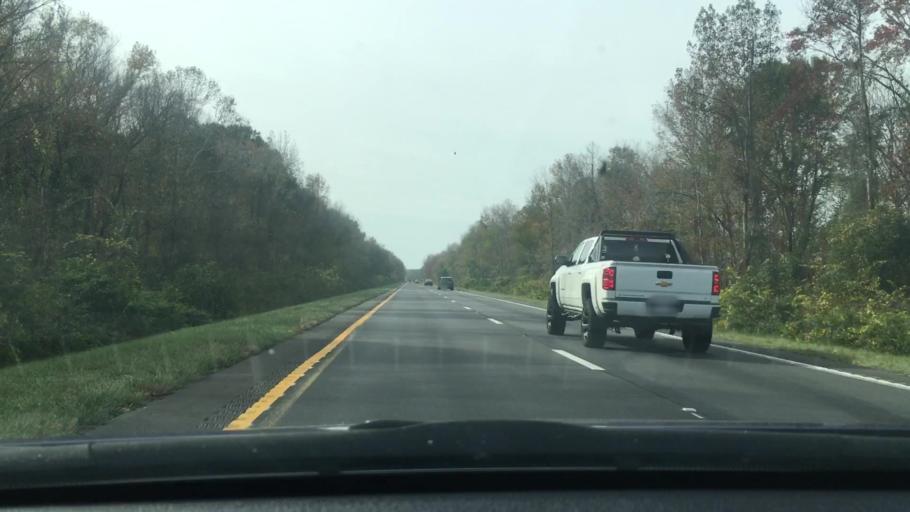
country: US
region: South Carolina
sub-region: Sumter County
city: Stateburg
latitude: 33.9504
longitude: -80.6014
